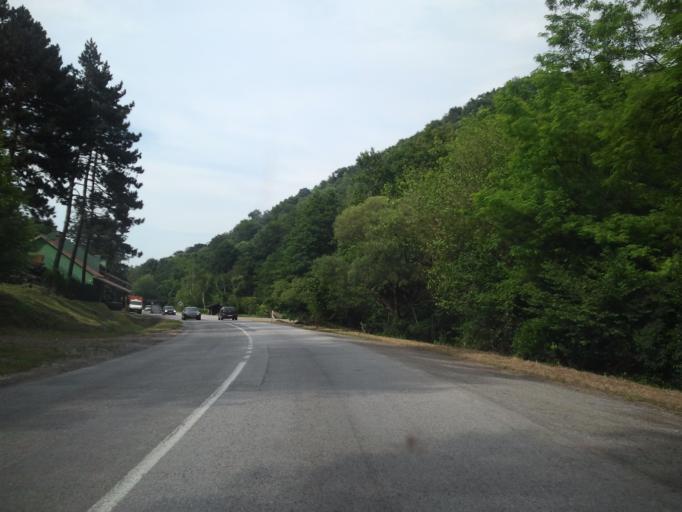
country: RS
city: Vrdnik
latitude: 45.1786
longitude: 19.8382
